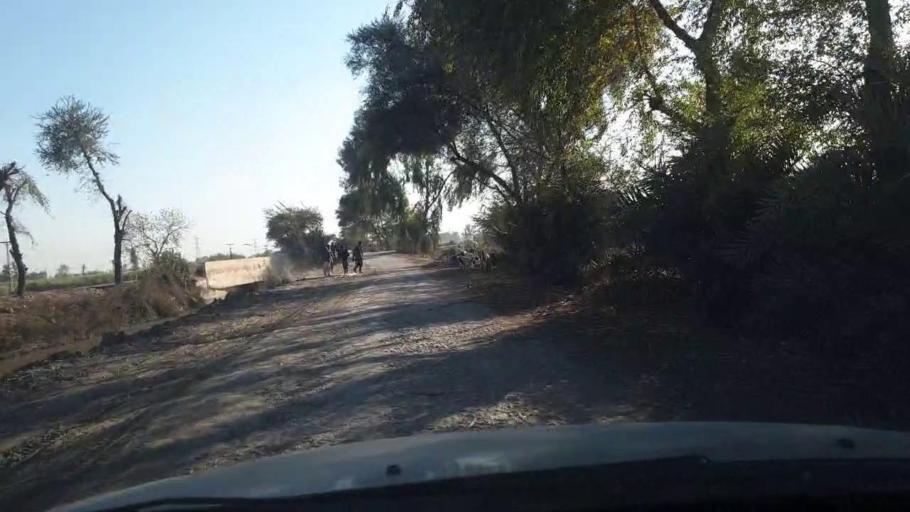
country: PK
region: Sindh
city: Ghotki
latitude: 28.0337
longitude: 69.3233
